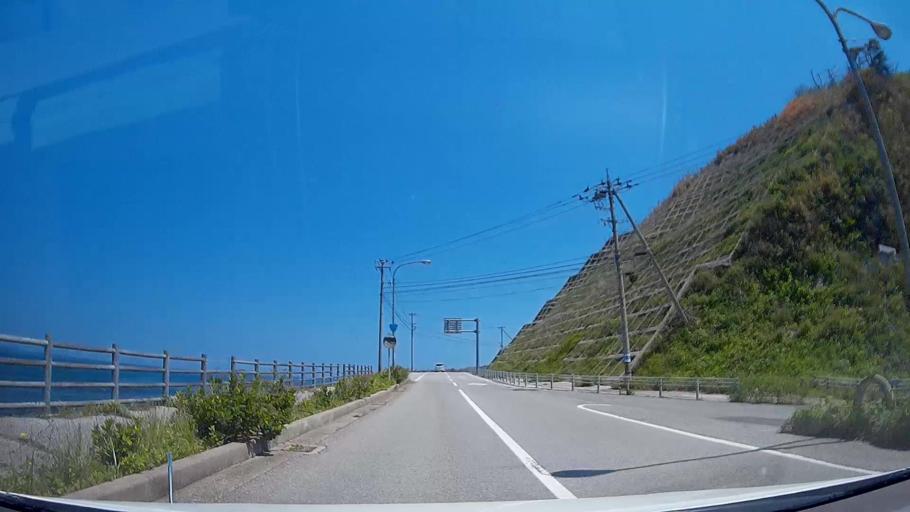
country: JP
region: Ishikawa
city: Nanao
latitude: 37.4338
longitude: 137.0315
